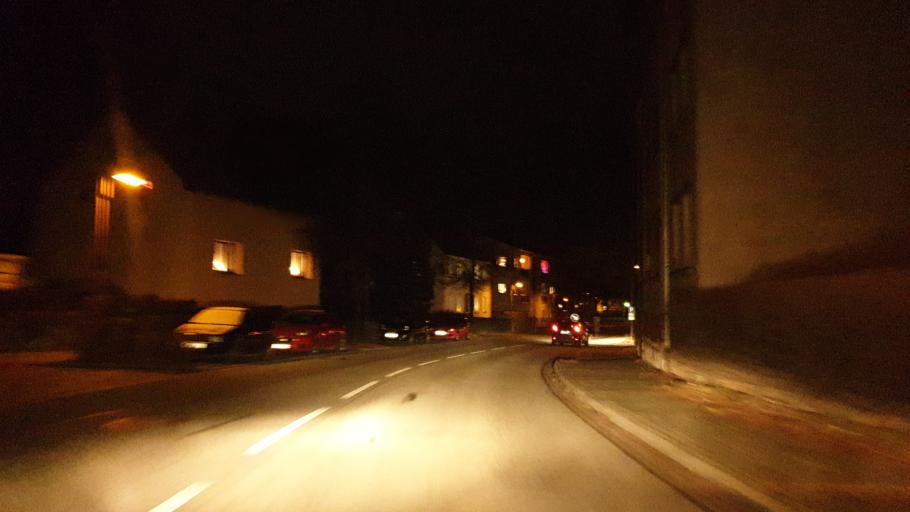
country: DE
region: Saxony
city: Lugau
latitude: 50.7221
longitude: 12.7464
